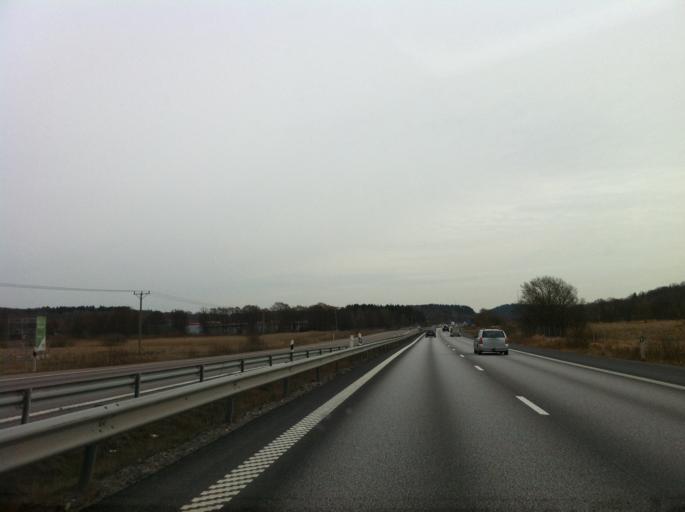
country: SE
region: Vaestra Goetaland
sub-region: Kungalvs Kommun
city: Kode
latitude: 57.9327
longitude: 11.8716
